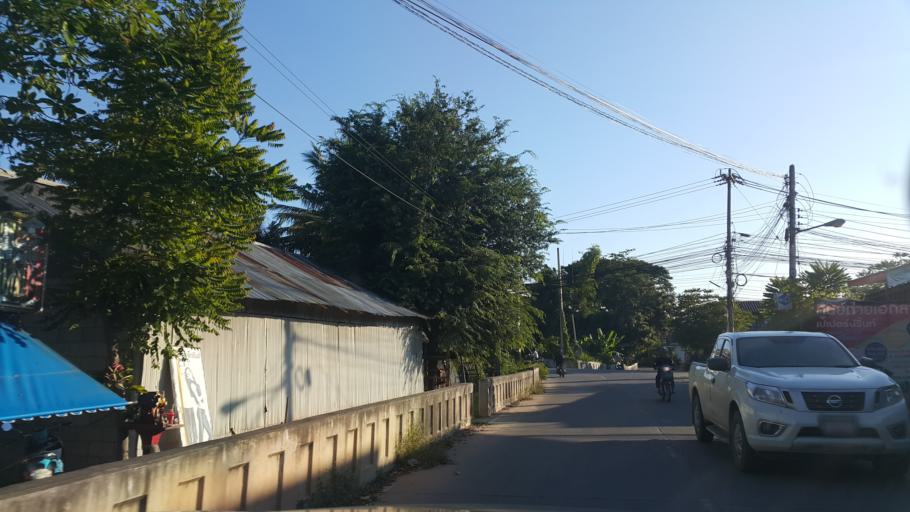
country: TH
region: Lamphun
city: Lamphun
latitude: 18.5982
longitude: 99.0306
